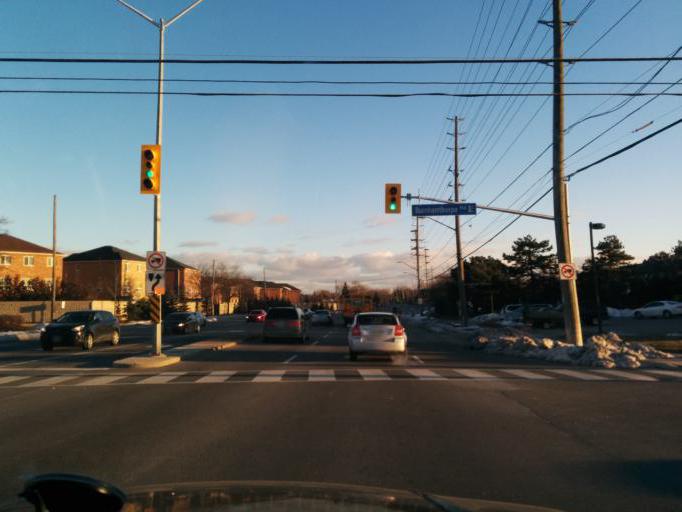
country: CA
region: Ontario
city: Mississauga
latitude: 43.6139
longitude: -79.6122
